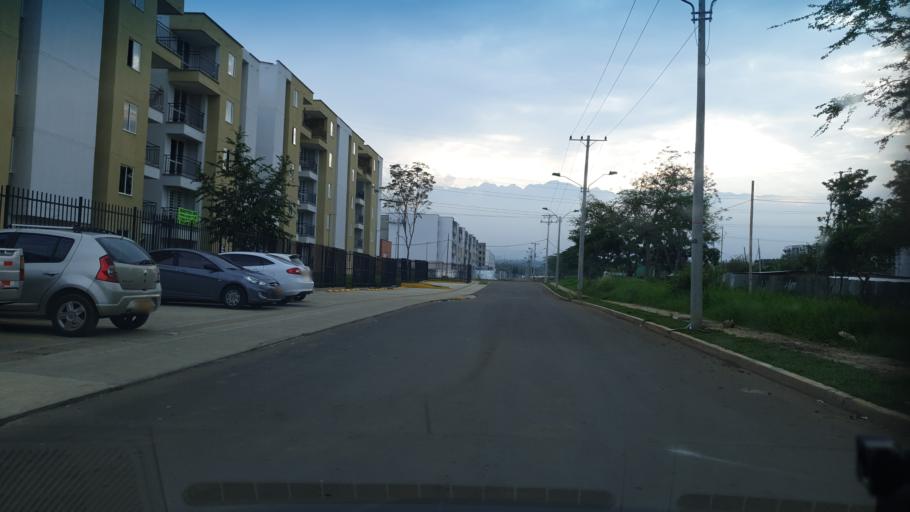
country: CO
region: Valle del Cauca
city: Jamundi
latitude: 3.3457
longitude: -76.5133
